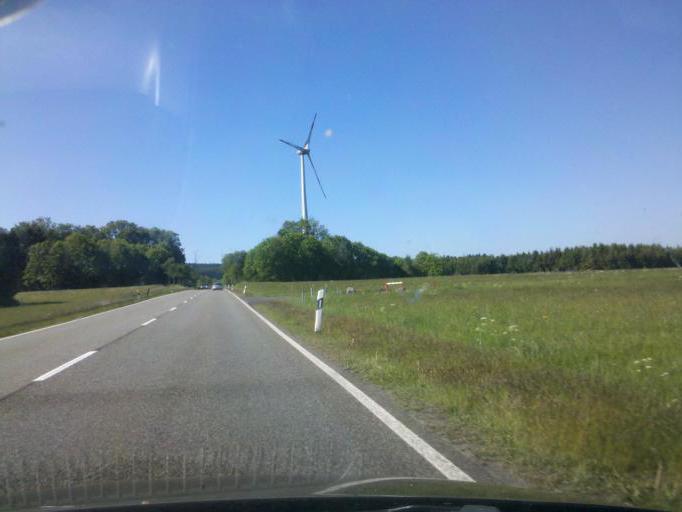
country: DE
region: Rheinland-Pfalz
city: Zehnhausen bei Rennerod
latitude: 50.6548
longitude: 8.0610
